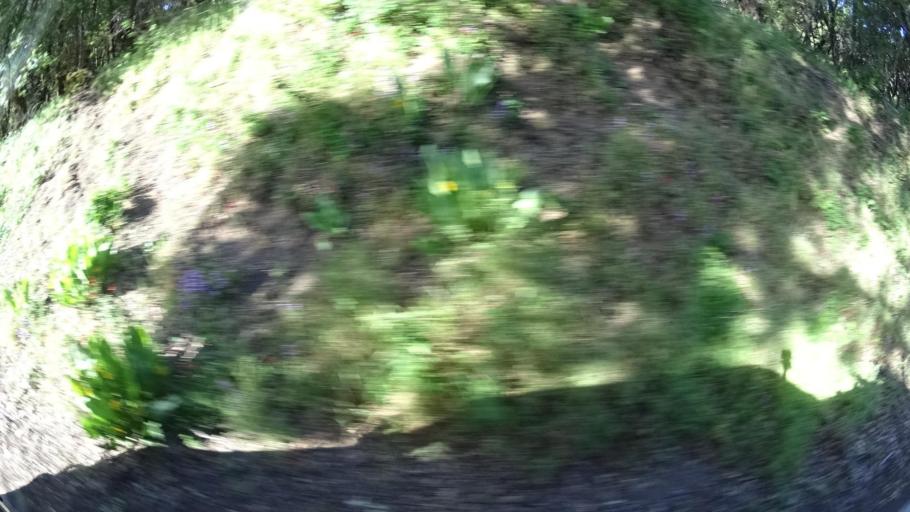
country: US
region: California
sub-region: Lake County
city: Upper Lake
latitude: 39.1367
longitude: -122.9991
